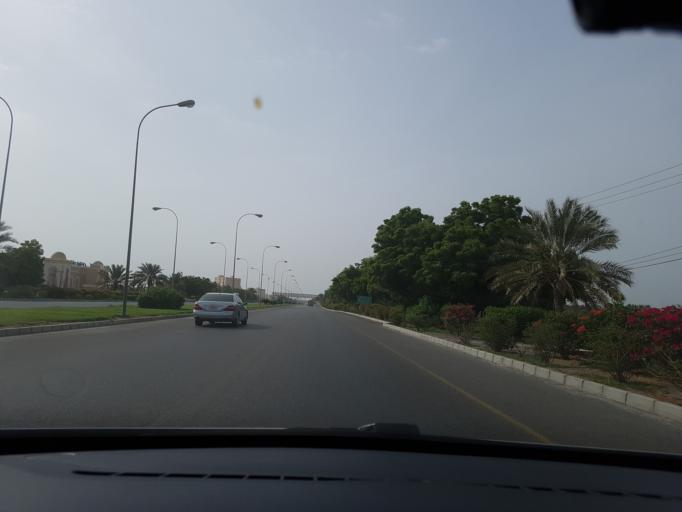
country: OM
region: Al Batinah
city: Al Sohar
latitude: 24.3638
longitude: 56.7079
